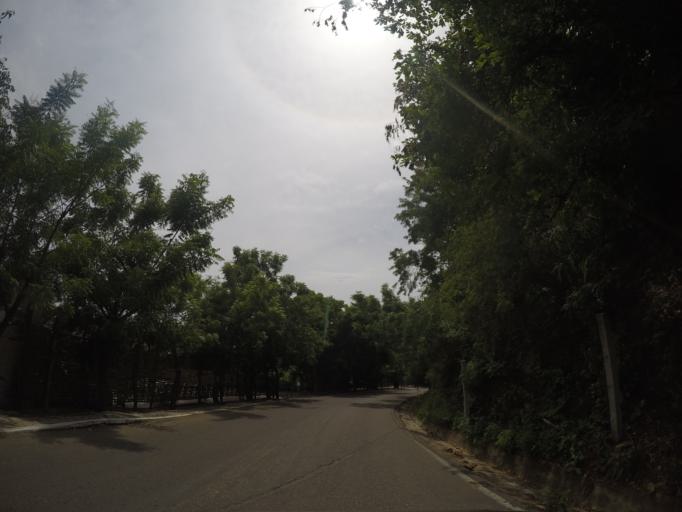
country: MX
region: Oaxaca
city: Santa Maria Tonameca
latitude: 15.6668
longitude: -96.5361
